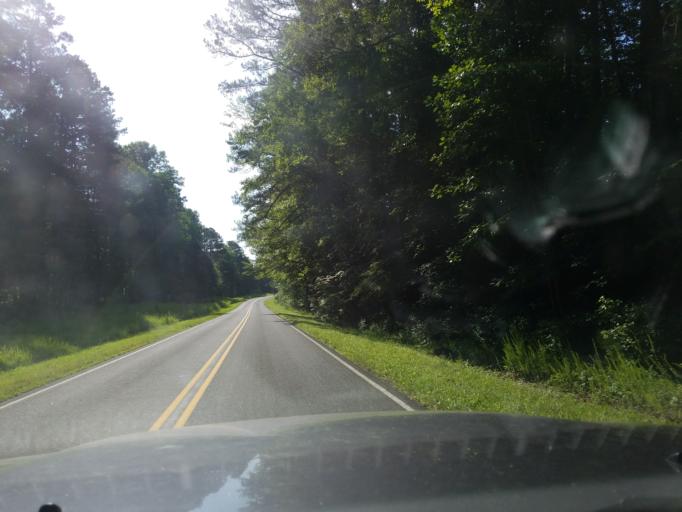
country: US
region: North Carolina
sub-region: Granville County
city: Butner
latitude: 36.1836
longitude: -78.8116
